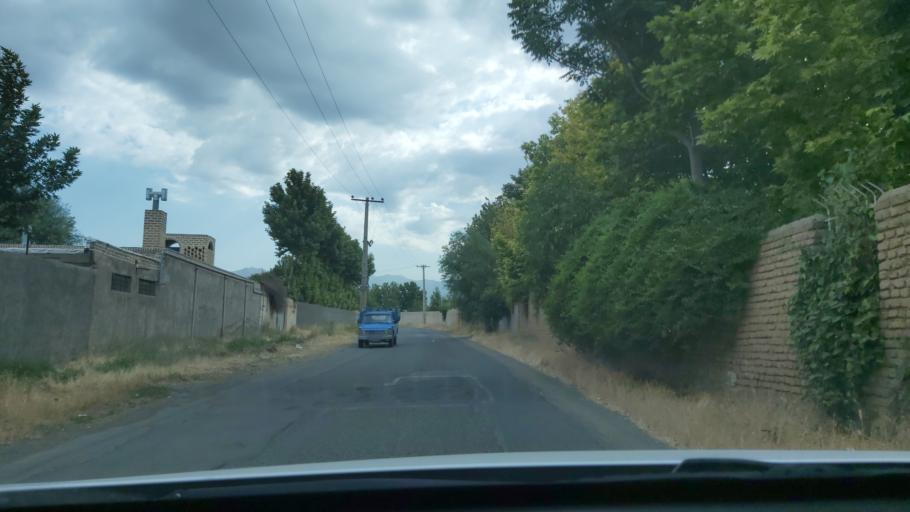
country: IR
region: Alborz
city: Hashtgerd
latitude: 35.9512
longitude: 50.7748
